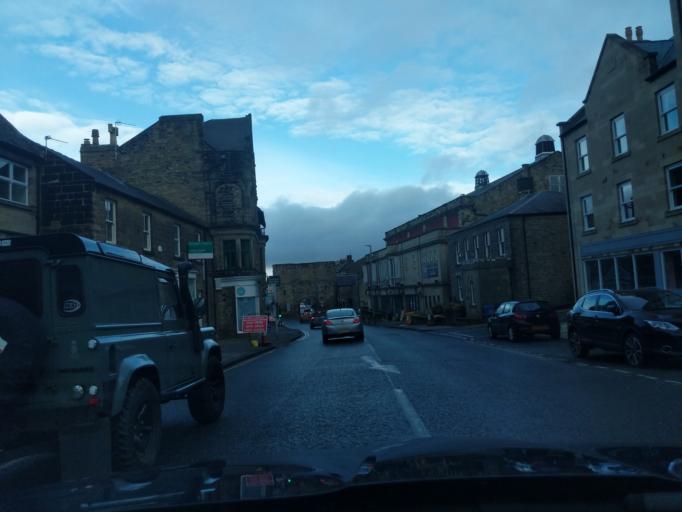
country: GB
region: England
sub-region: Northumberland
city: Alnwick
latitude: 55.4119
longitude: -1.7022
